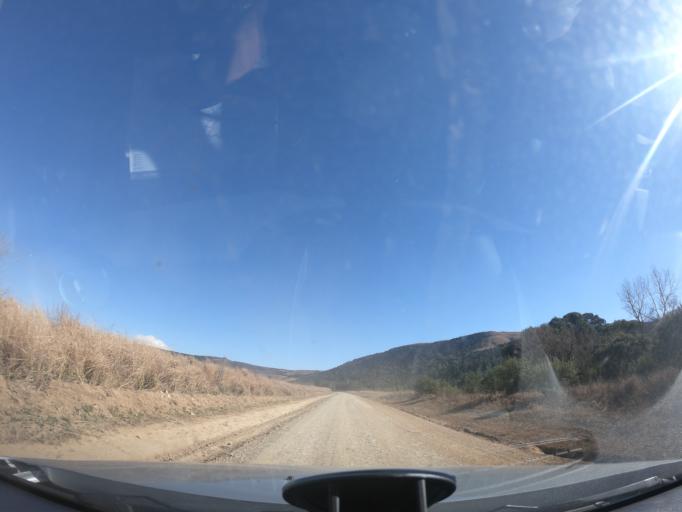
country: ZA
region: KwaZulu-Natal
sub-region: uMgungundlovu District Municipality
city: Impendle
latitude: -29.4174
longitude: 29.9270
